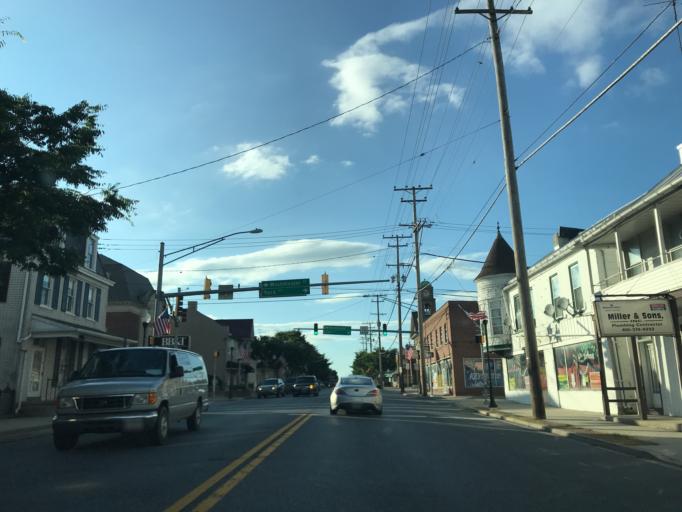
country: US
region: Maryland
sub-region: Carroll County
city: Manchester
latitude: 39.6609
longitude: -76.8846
